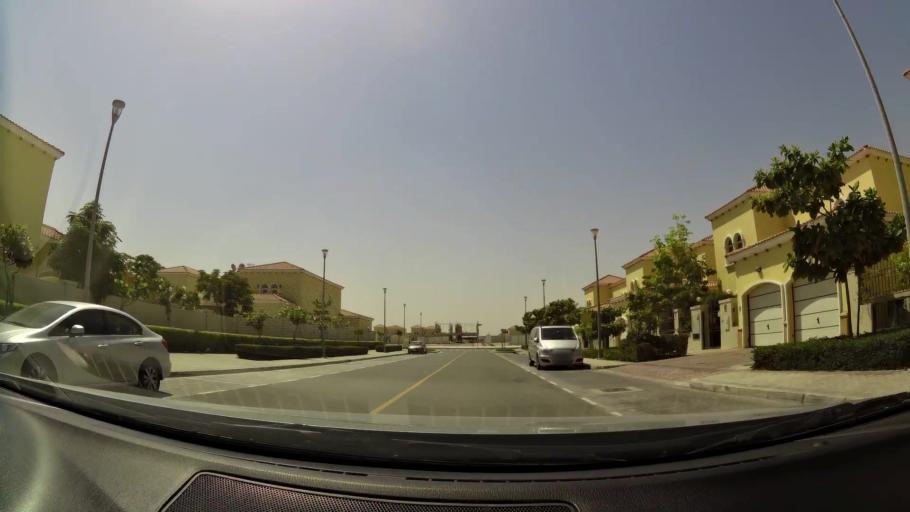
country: AE
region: Dubai
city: Dubai
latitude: 25.0522
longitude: 55.1516
